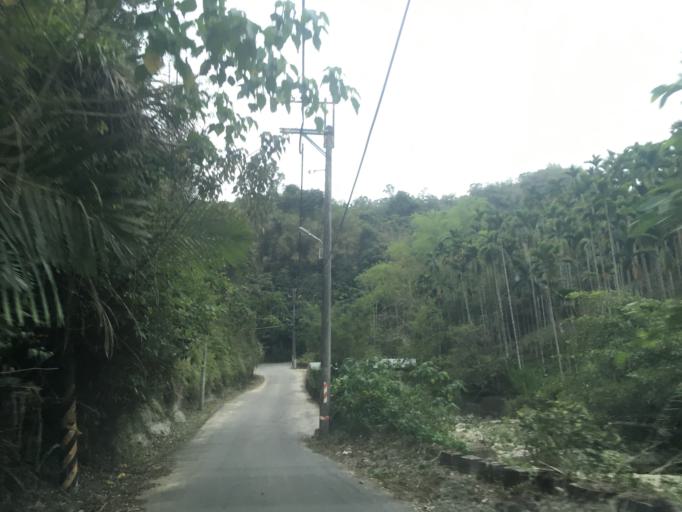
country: TW
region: Taiwan
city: Zhongxing New Village
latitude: 24.0380
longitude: 120.7527
